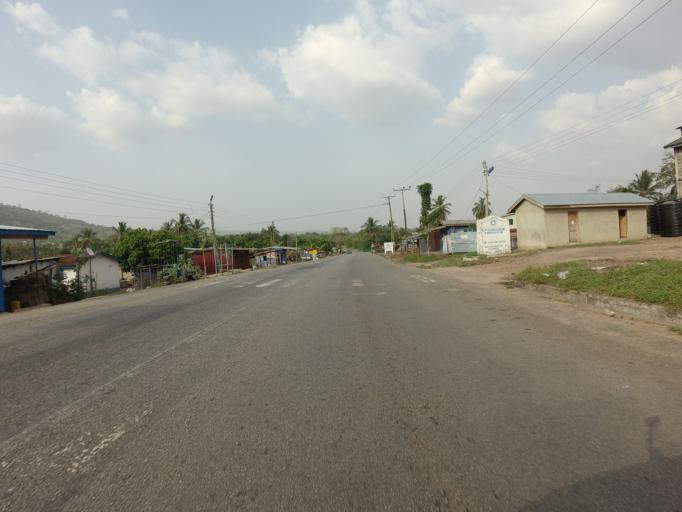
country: GH
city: Akropong
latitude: 6.2579
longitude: 0.1347
